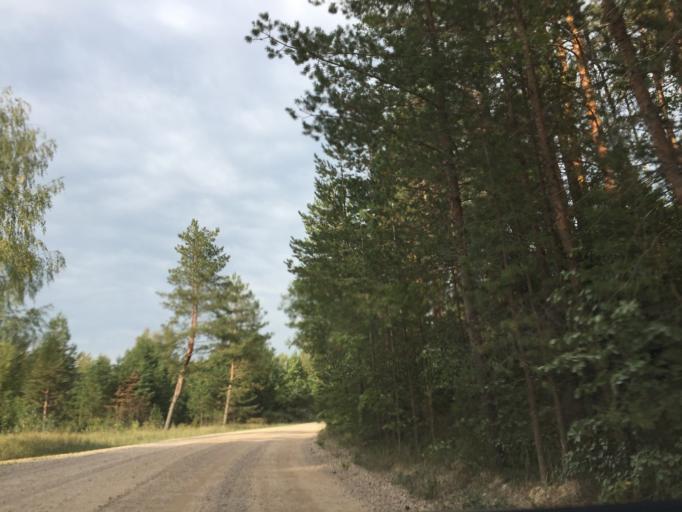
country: LV
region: Ikskile
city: Ikskile
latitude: 56.8060
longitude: 24.4409
